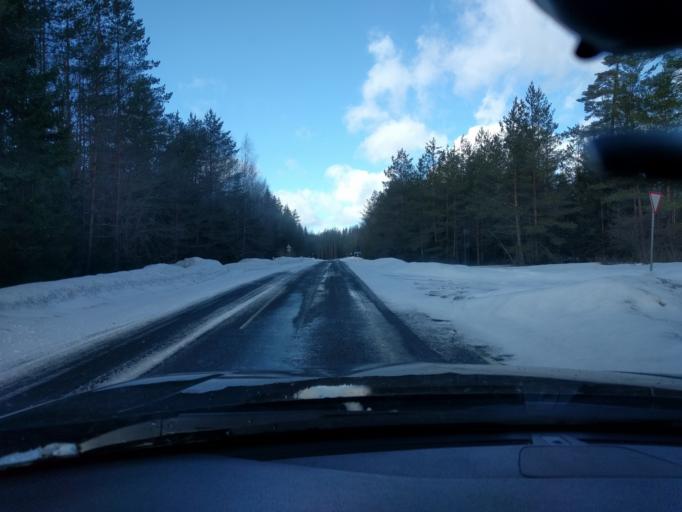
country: EE
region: Harju
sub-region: Anija vald
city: Kehra
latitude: 59.2202
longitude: 25.4468
